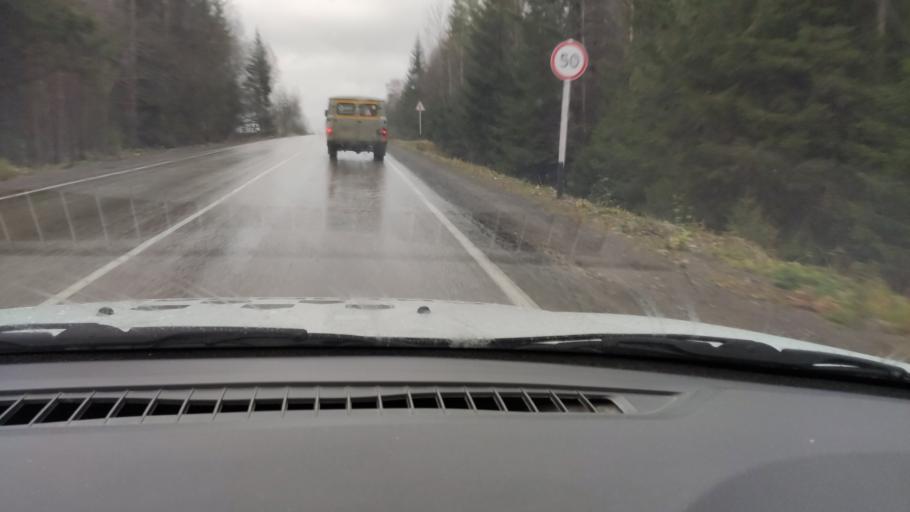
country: RU
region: Perm
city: Novyye Lyady
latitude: 58.0285
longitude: 56.6836
